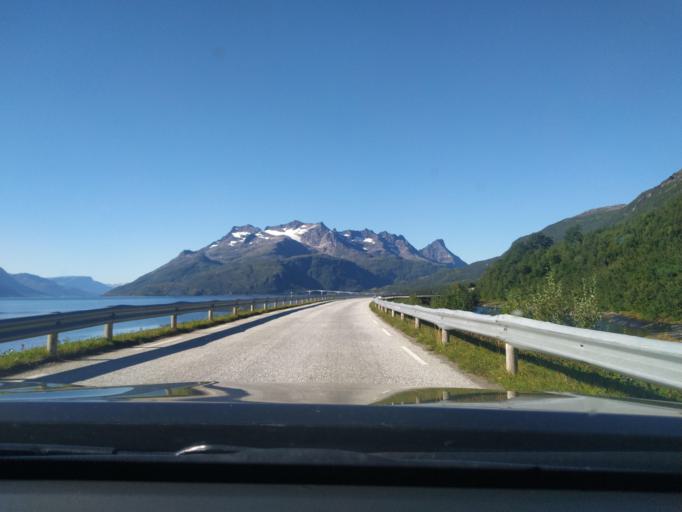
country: NO
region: Troms
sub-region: Dyroy
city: Brostadbotn
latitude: 68.9149
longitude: 17.5788
